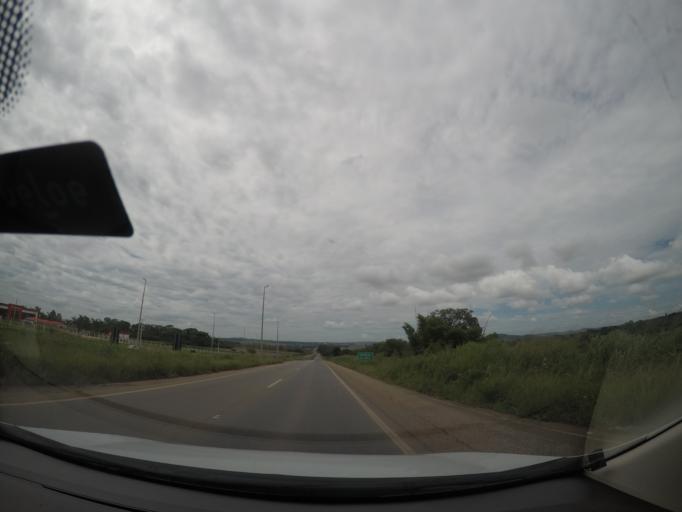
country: BR
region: Goias
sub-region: Goianira
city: Goianira
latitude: -16.4671
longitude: -49.4397
